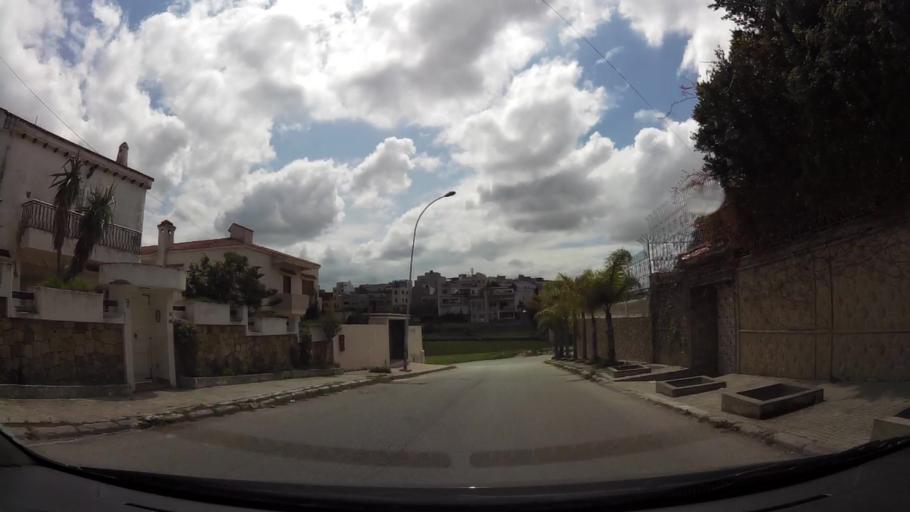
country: MA
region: Tanger-Tetouan
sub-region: Tanger-Assilah
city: Tangier
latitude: 35.7735
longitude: -5.7730
